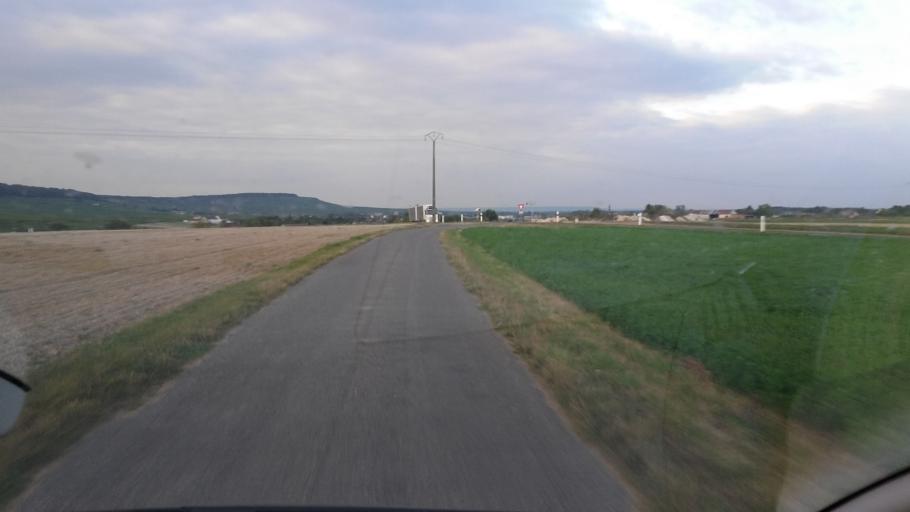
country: FR
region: Champagne-Ardenne
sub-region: Departement de la Marne
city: Vertus
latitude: 48.8722
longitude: 3.9986
